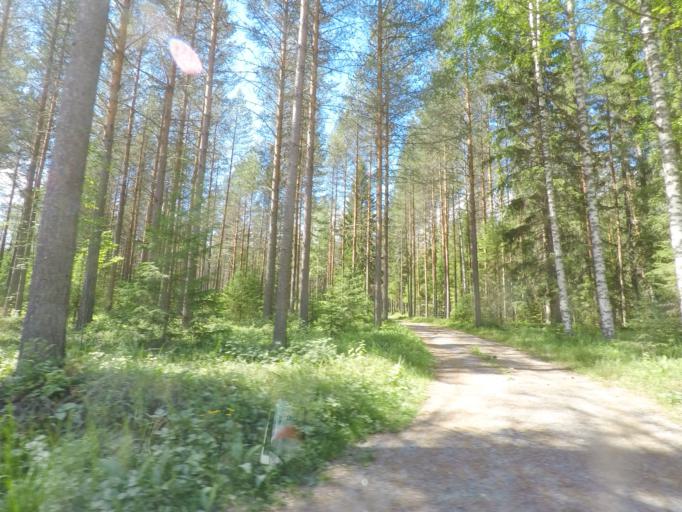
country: FI
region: Central Finland
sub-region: Jyvaeskylae
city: Hankasalmi
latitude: 62.4359
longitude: 26.6472
